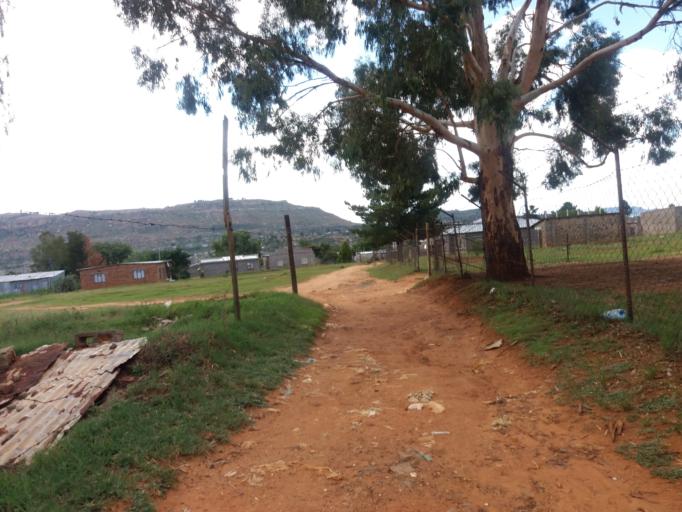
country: LS
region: Maseru
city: Maseru
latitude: -29.3696
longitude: 27.5064
